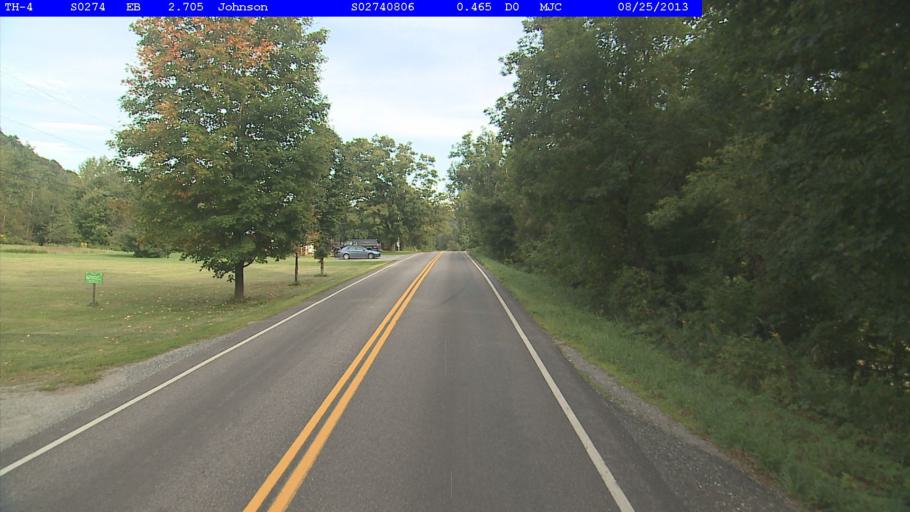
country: US
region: Vermont
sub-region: Lamoille County
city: Johnson
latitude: 44.6544
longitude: -72.7422
